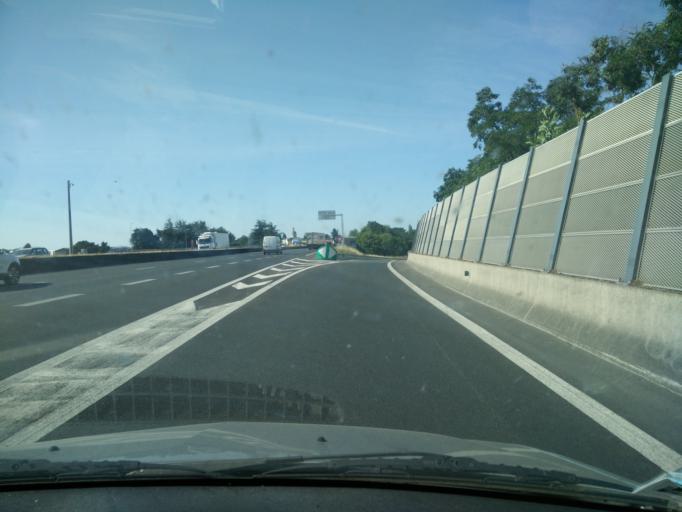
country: FR
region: Pays de la Loire
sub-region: Departement de Maine-et-Loire
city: Angers
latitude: 47.4624
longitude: -0.5172
